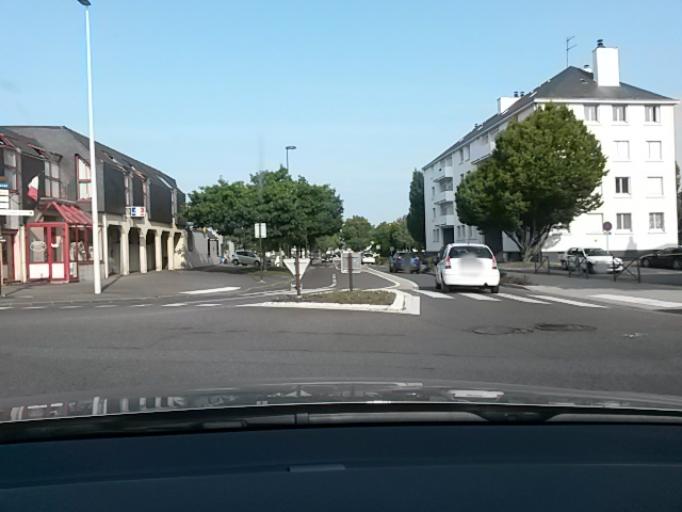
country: FR
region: Pays de la Loire
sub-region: Departement de la Loire-Atlantique
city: Guerande
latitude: 47.3303
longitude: -2.4244
